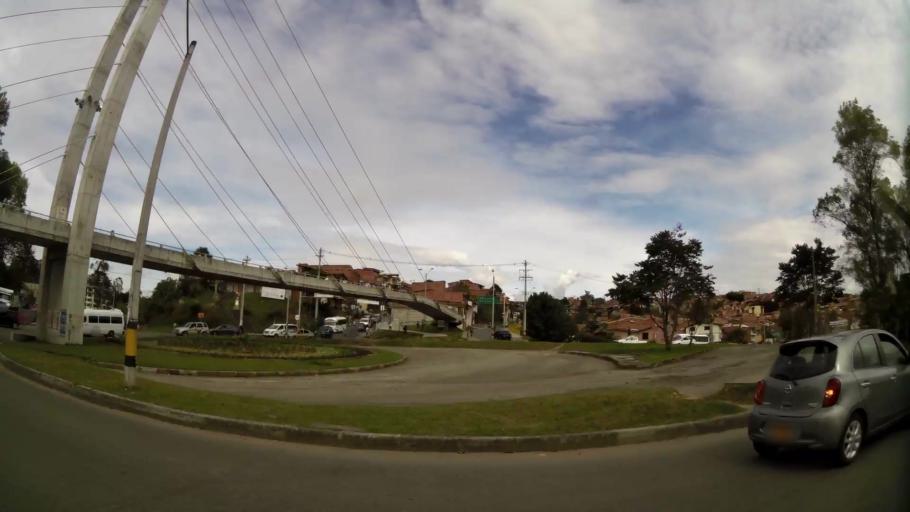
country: CO
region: Antioquia
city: Rionegro
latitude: 6.1549
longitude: -75.3678
